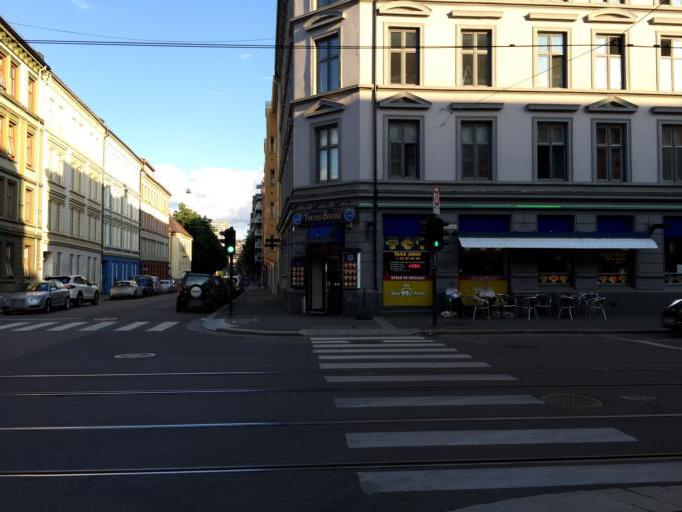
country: NO
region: Oslo
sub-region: Oslo
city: Oslo
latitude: 59.9191
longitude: 10.7625
